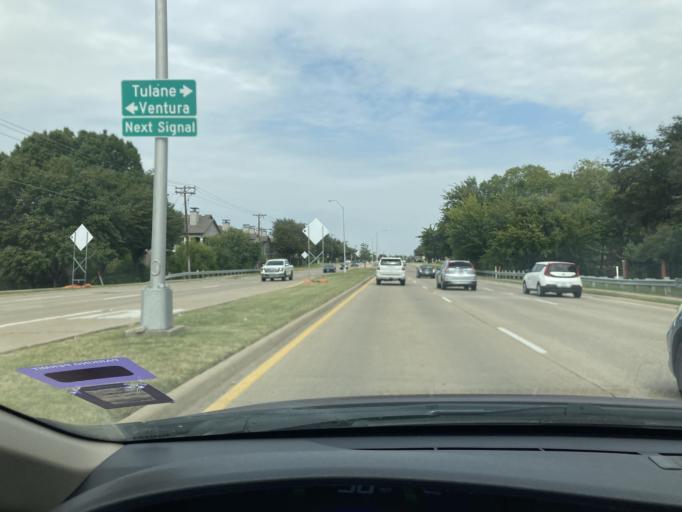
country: US
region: Texas
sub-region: Dallas County
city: Addison
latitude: 33.0326
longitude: -96.7947
